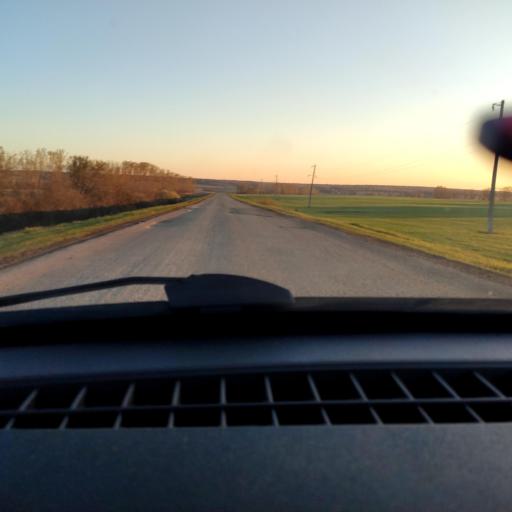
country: RU
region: Bashkortostan
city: Chishmy
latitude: 54.4633
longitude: 55.5410
